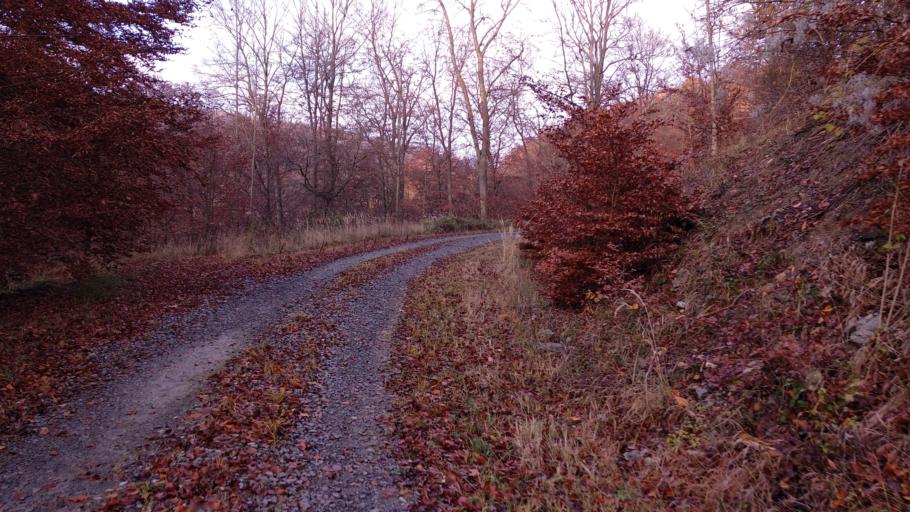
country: DE
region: North Rhine-Westphalia
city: Beverungen
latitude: 51.6575
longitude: 9.3220
